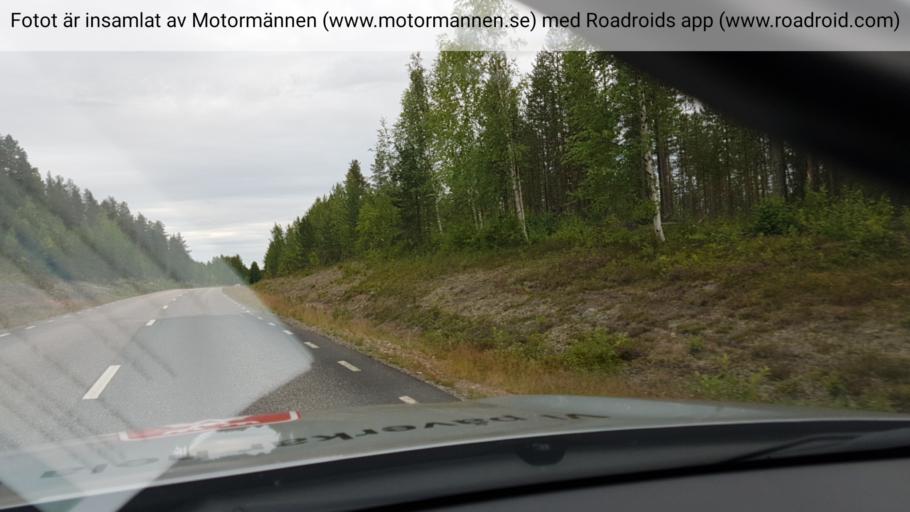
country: SE
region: Norrbotten
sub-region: Overkalix Kommun
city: OEverkalix
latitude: 66.5203
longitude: 22.7651
